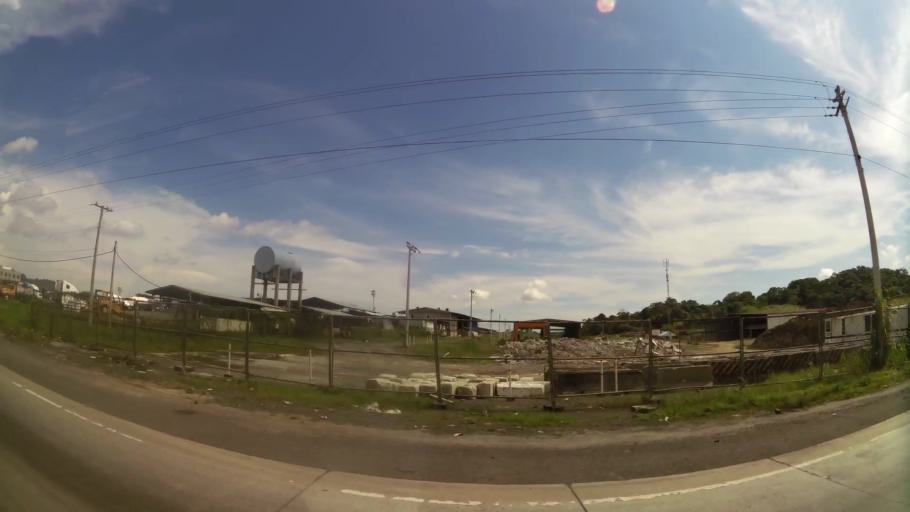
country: PA
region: Panama
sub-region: Distrito de Panama
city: Paraiso
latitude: 9.0307
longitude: -79.5844
